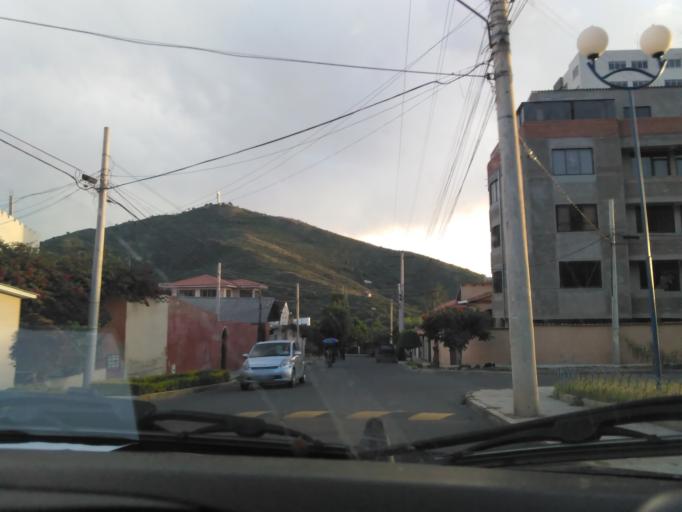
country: BO
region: Cochabamba
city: Cochabamba
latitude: -17.3729
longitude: -66.1377
